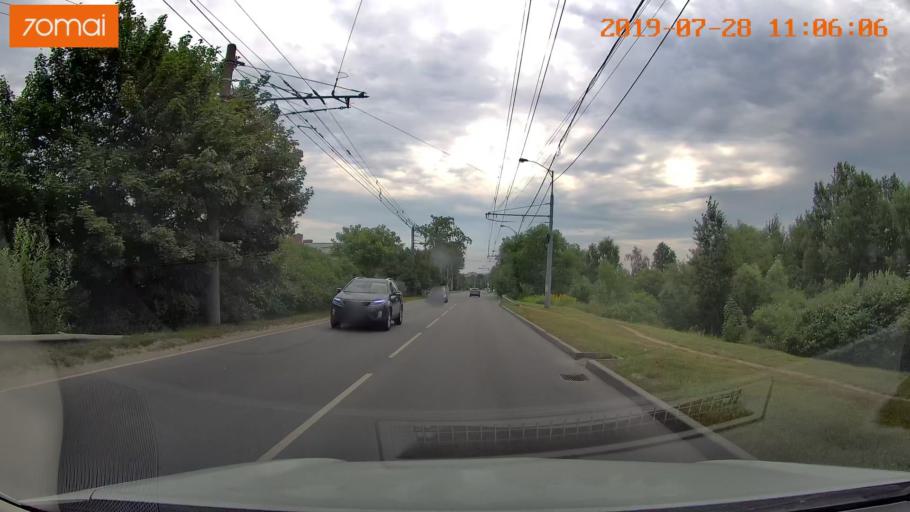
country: RU
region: Kaliningrad
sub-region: Gorod Kaliningrad
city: Kaliningrad
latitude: 54.7155
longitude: 20.4048
